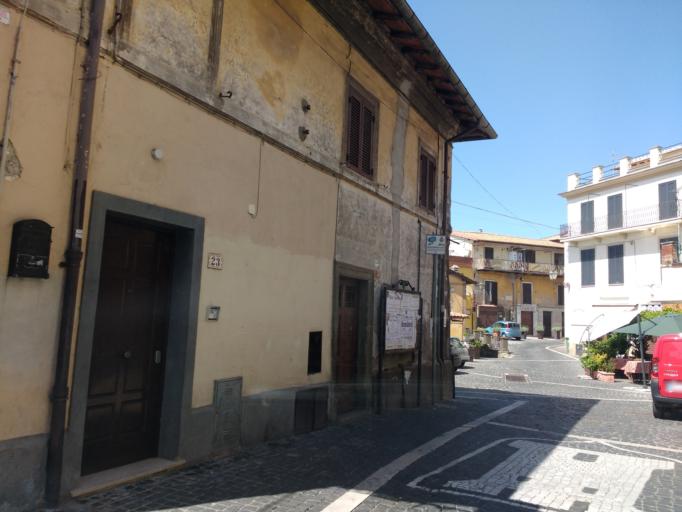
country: IT
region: Latium
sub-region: Citta metropolitana di Roma Capitale
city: Rocca di Papa
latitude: 41.7607
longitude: 12.7088
